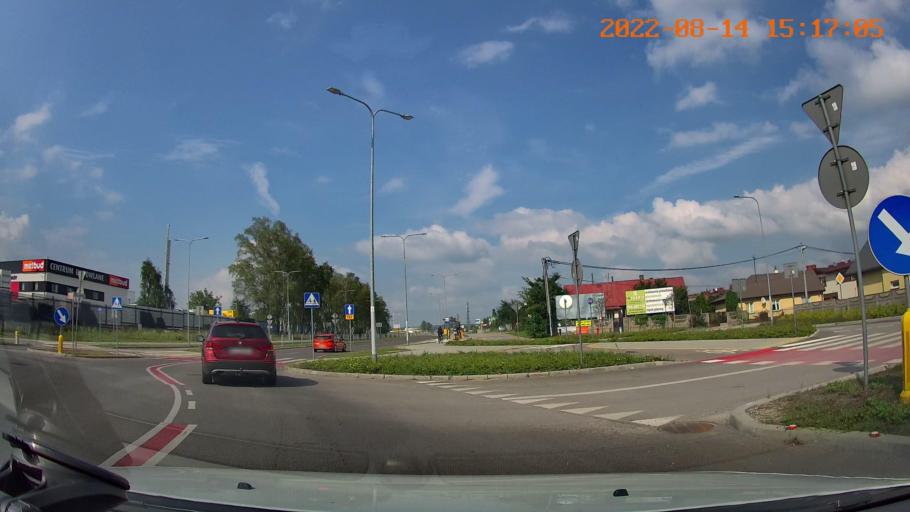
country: PL
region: Swietokrzyskie
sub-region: Powiat kielecki
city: Kielce
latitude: 50.8963
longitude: 20.6326
